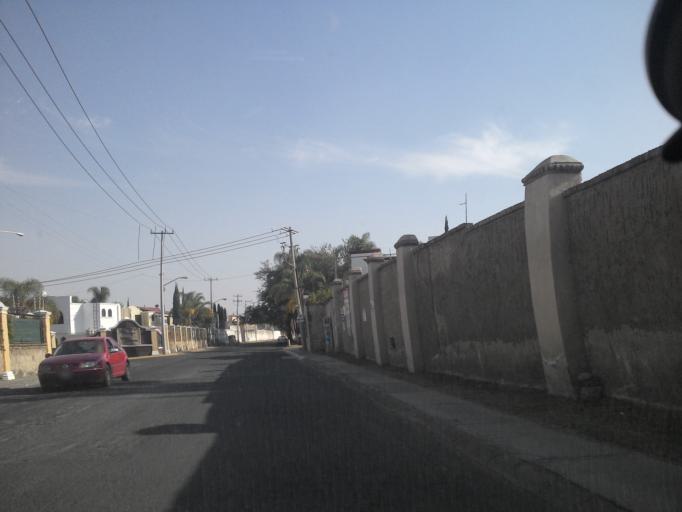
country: MX
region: Jalisco
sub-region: Tlajomulco de Zuniga
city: Palomar
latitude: 20.6090
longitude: -103.4525
